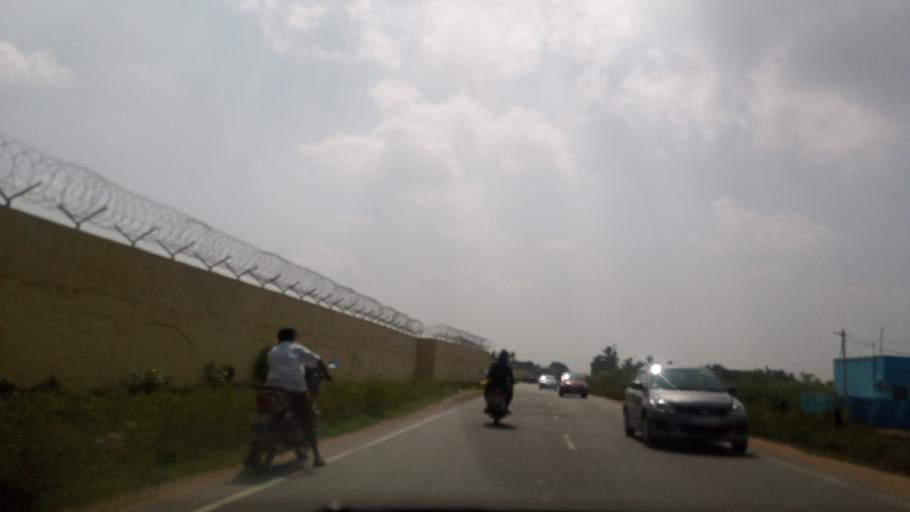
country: IN
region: Tamil Nadu
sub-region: Vellore
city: Arakkonam
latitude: 13.0613
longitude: 79.6737
